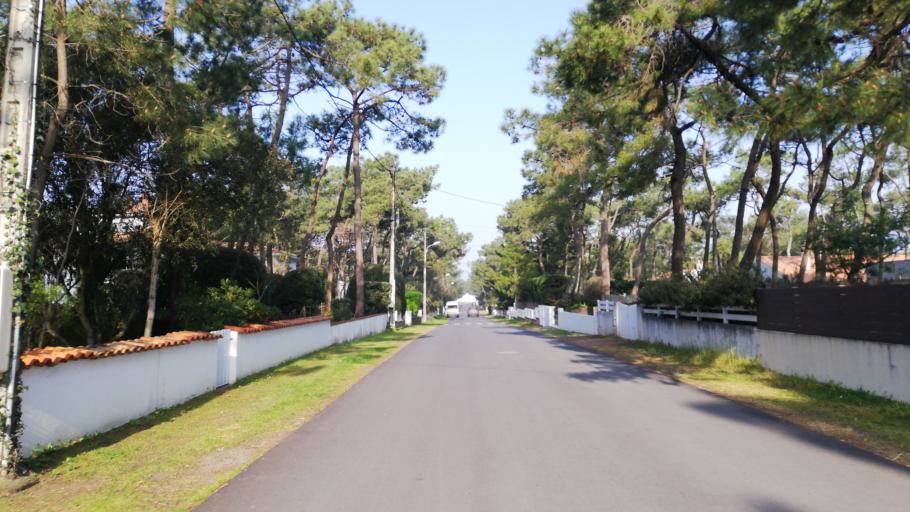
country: FR
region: Pays de la Loire
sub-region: Departement de la Vendee
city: La Tranche-sur-Mer
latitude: 46.3465
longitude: -1.4132
